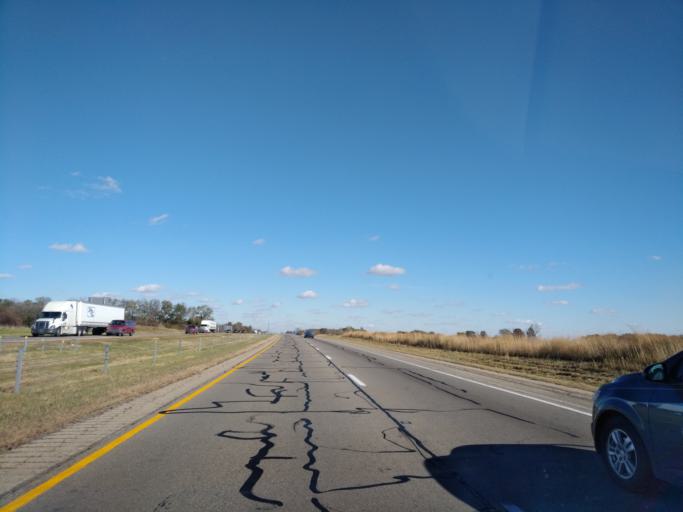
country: US
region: Indiana
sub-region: Hancock County
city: Greenfield
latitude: 39.8214
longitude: -85.7405
